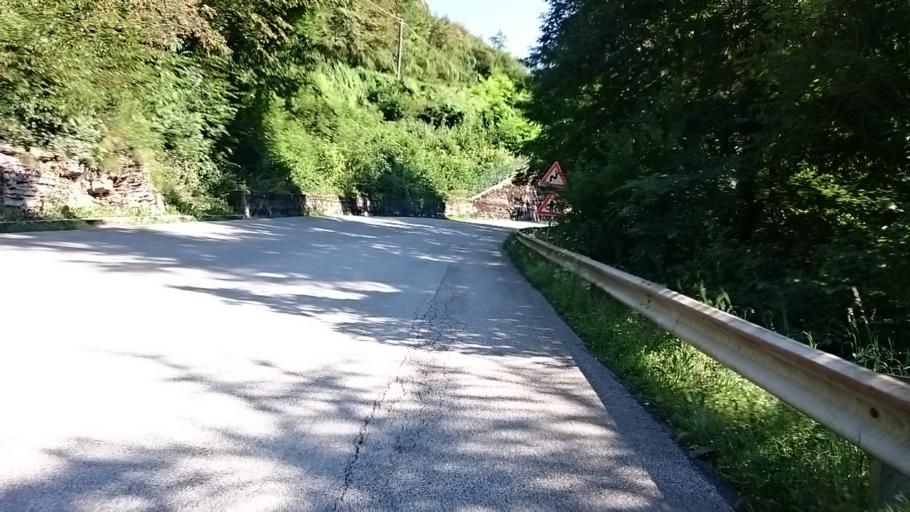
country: IT
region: Veneto
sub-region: Provincia di Belluno
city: Longarone
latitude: 46.2647
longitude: 12.3128
